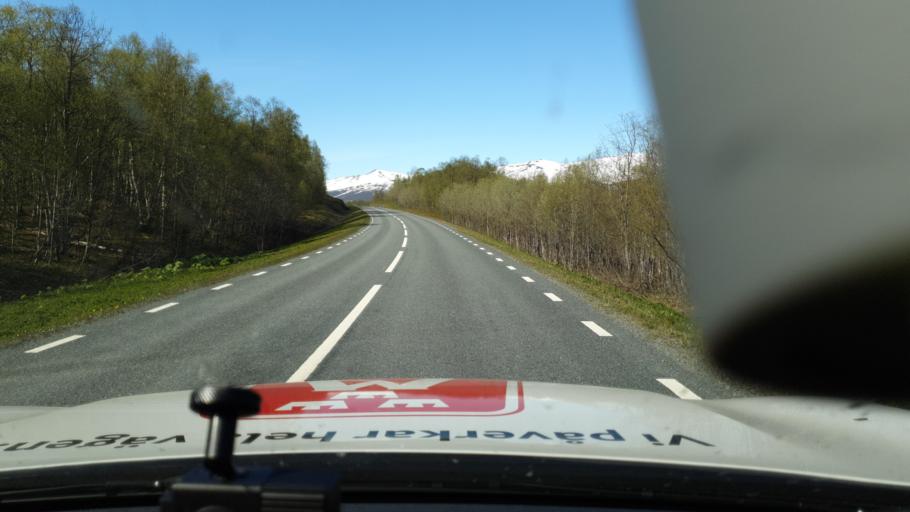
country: NO
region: Nordland
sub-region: Rana
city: Mo i Rana
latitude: 65.7610
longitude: 15.1163
